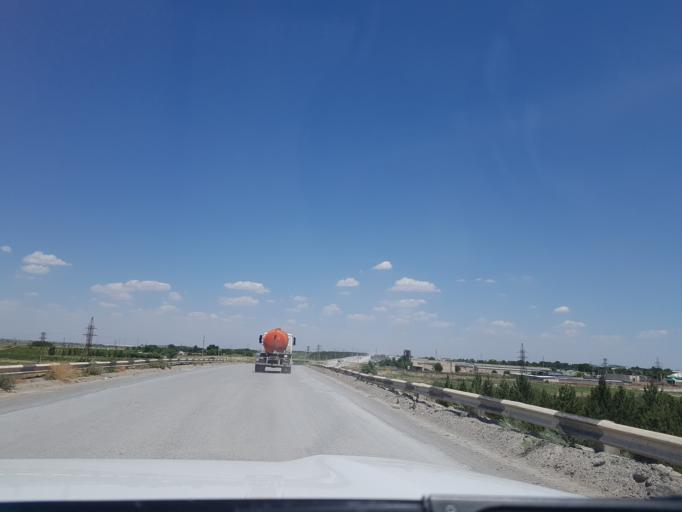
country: TM
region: Ahal
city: Abadan
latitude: 38.1722
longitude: 57.9417
